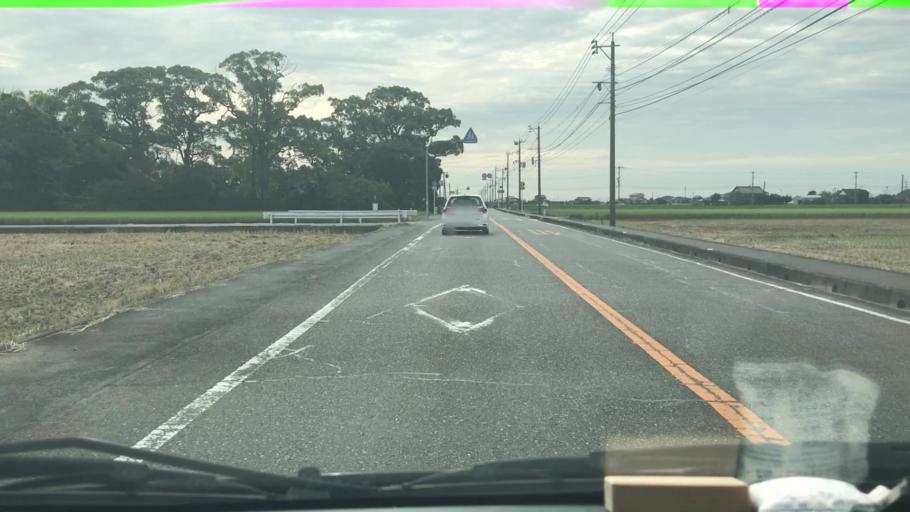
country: JP
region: Saga Prefecture
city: Takeocho-takeo
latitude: 33.2039
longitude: 130.0932
